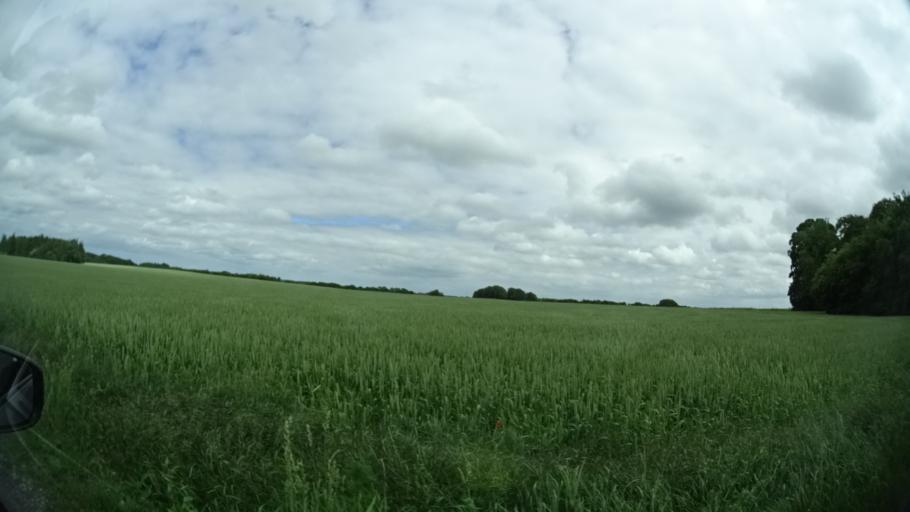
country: DK
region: Central Jutland
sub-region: Syddjurs Kommune
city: Ryomgard
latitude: 56.3980
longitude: 10.5625
